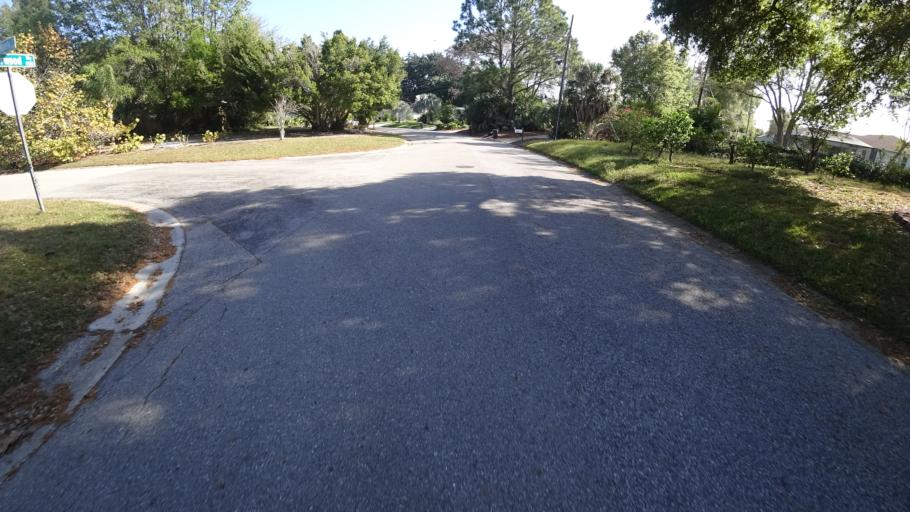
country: US
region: Florida
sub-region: Manatee County
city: Whitfield
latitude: 27.4165
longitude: -82.5573
